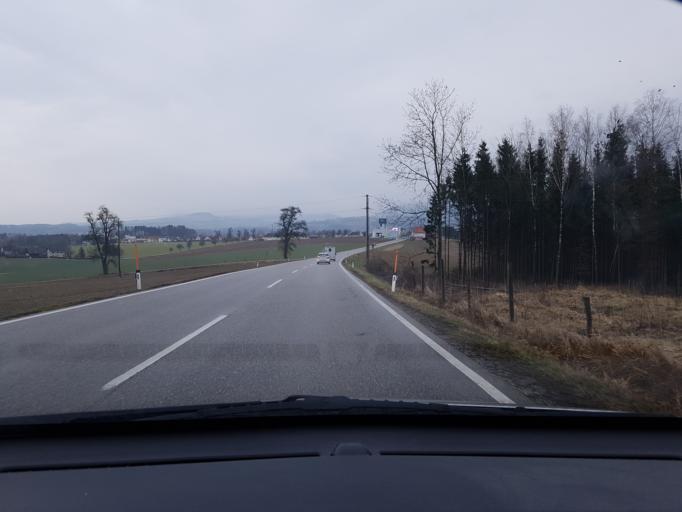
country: AT
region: Upper Austria
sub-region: Steyr Stadt
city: Steyr
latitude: 48.0556
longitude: 14.3902
